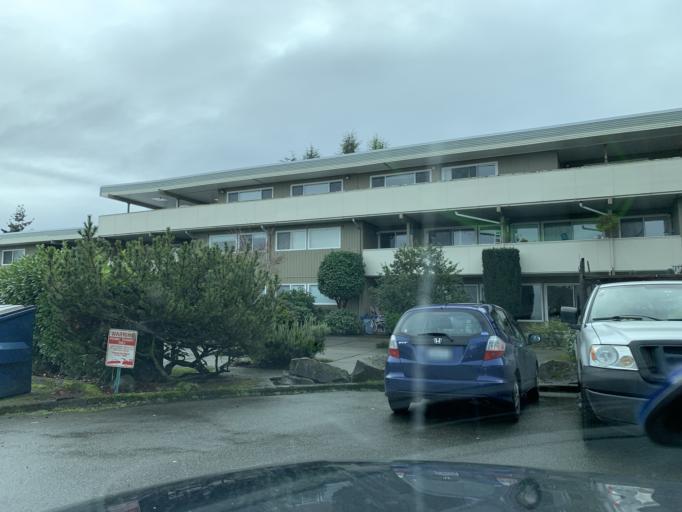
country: US
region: Washington
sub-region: King County
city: Mercer Island
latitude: 47.5848
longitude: -122.2384
